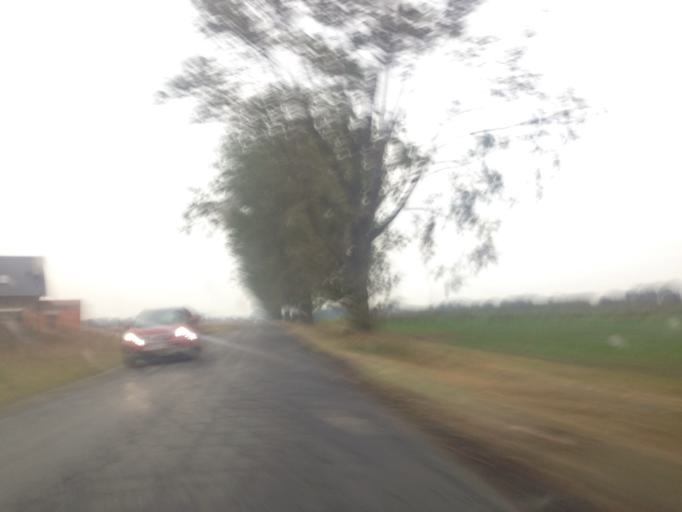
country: PL
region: Greater Poland Voivodeship
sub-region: Powiat poznanski
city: Kleszczewo
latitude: 52.3520
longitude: 17.1460
